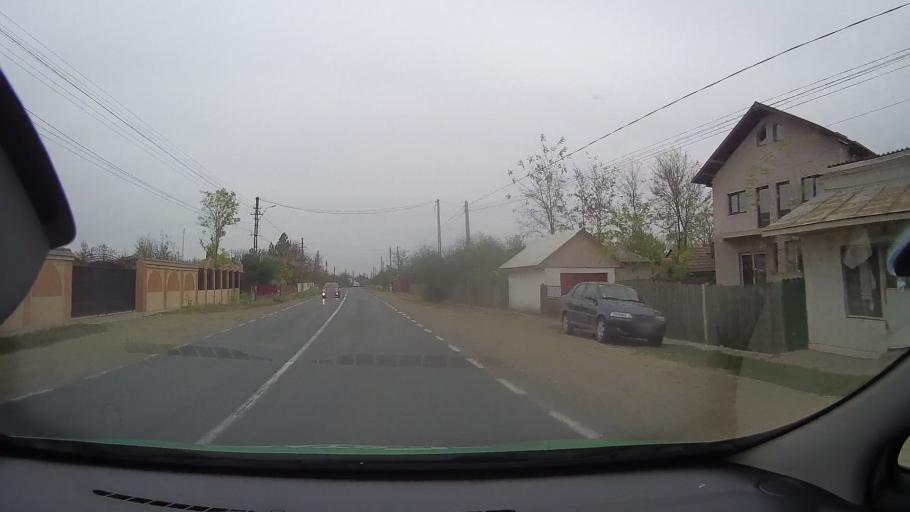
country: RO
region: Braila
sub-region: Comuna Baraganul
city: Baraganul
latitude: 44.8101
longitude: 27.5137
